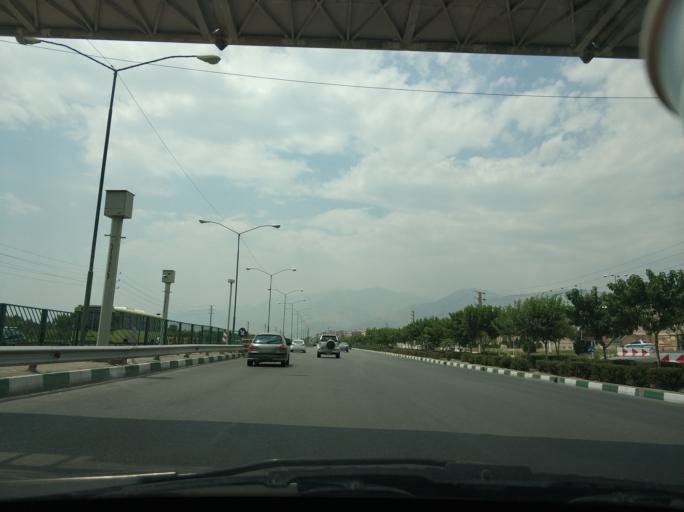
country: IR
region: Tehran
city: Tajrish
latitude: 35.7614
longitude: 51.5705
